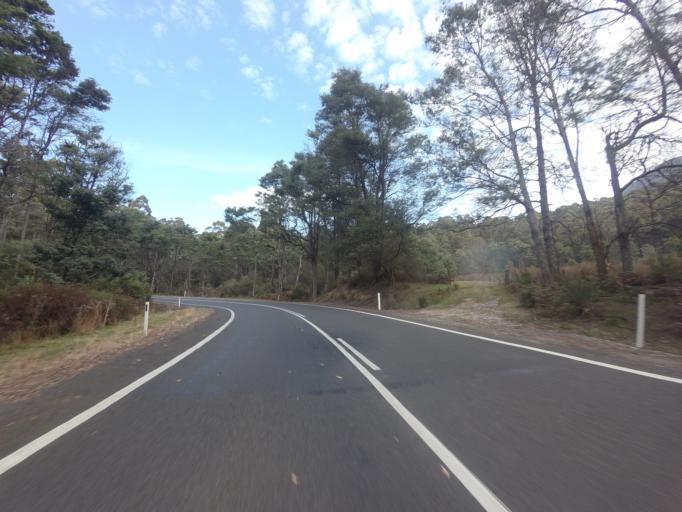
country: AU
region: Tasmania
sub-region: Meander Valley
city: Deloraine
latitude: -41.6393
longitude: 146.7149
